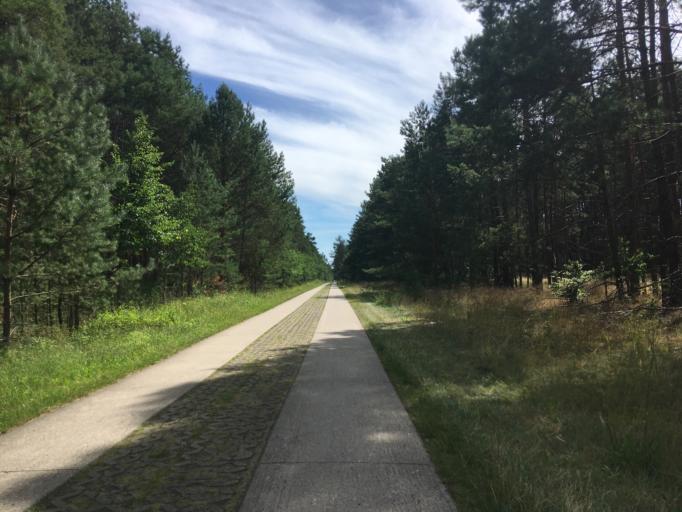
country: DE
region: Brandenburg
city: Rheinsberg
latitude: 53.0513
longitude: 12.9067
